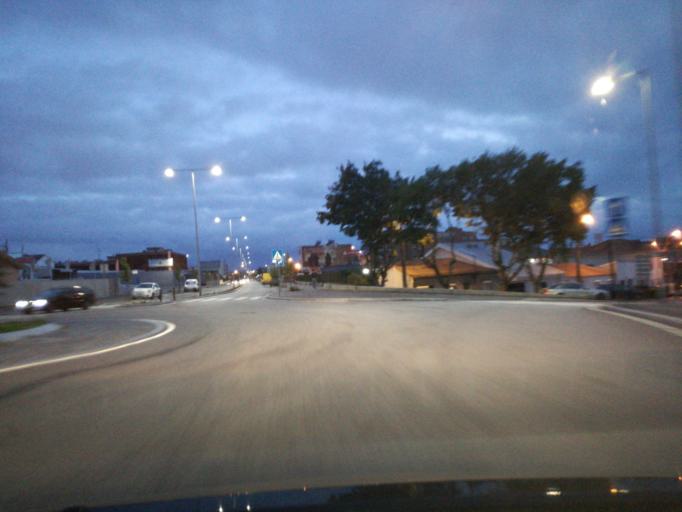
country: PT
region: Porto
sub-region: Matosinhos
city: Santa Cruz do Bispo
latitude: 41.2258
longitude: -8.6814
